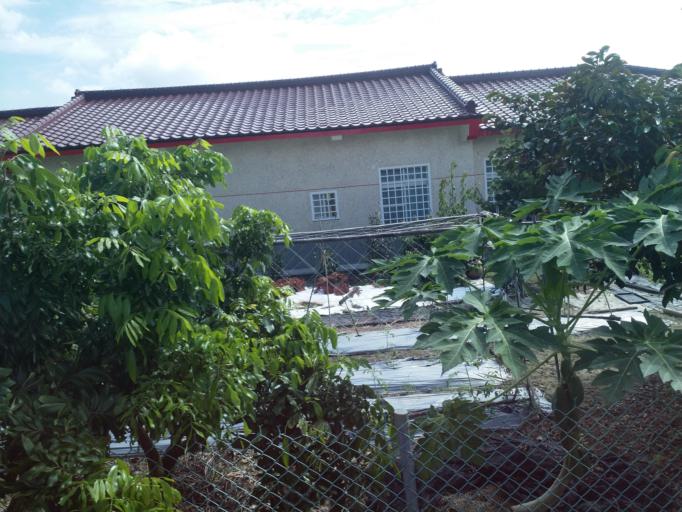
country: TW
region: Taiwan
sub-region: Pingtung
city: Pingtung
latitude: 22.8994
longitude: 120.5177
